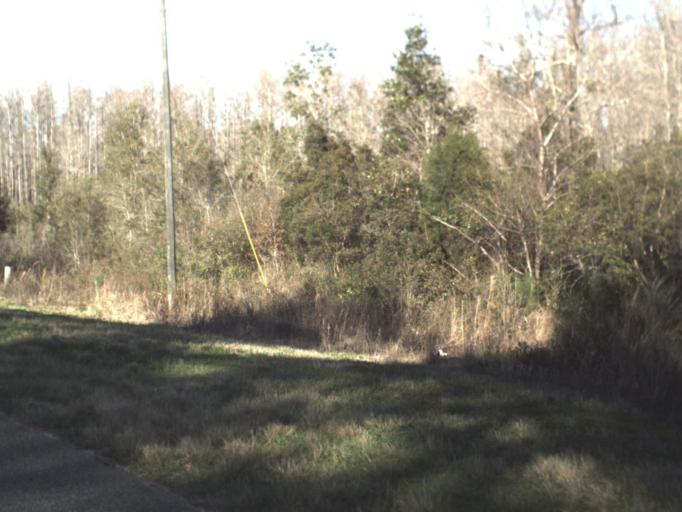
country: US
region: Florida
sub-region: Jackson County
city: Marianna
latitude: 30.6078
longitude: -85.1811
